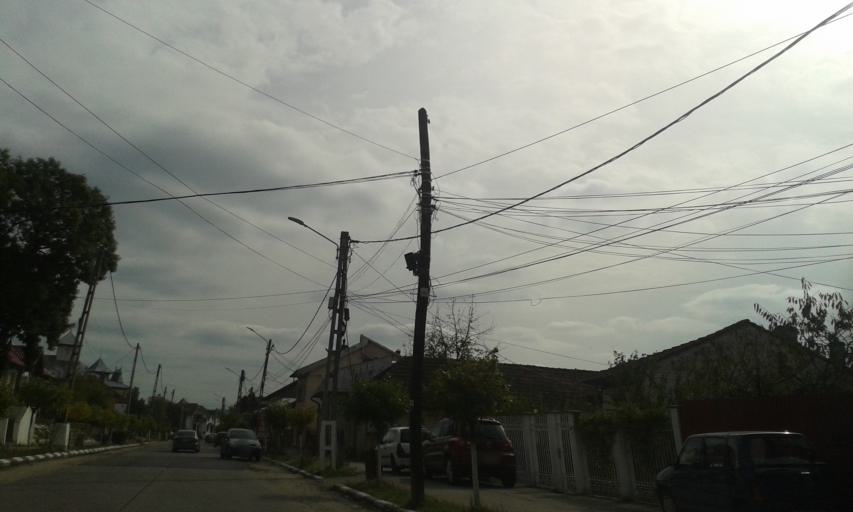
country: RO
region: Gorj
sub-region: Comuna Targu Carbunesti
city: Targu Carbunesti
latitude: 44.9573
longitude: 23.5119
